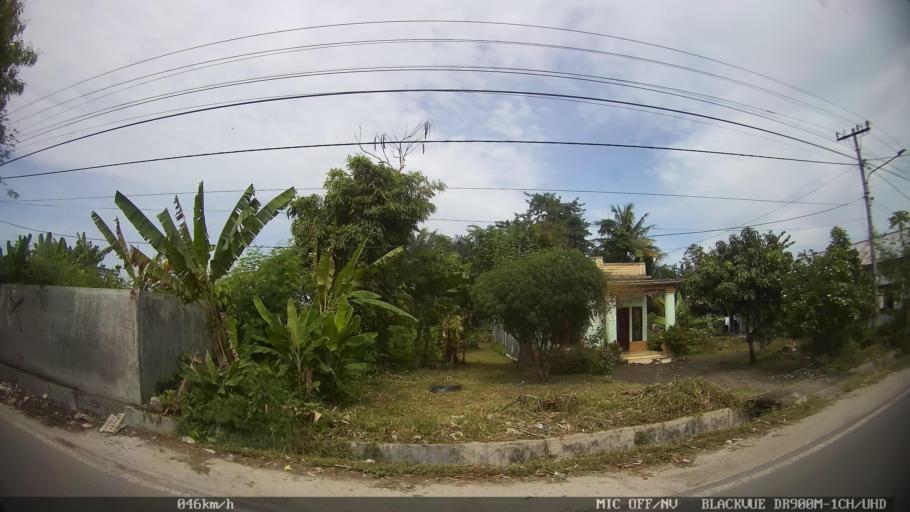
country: ID
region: North Sumatra
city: Percut
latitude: 3.6181
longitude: 98.7992
